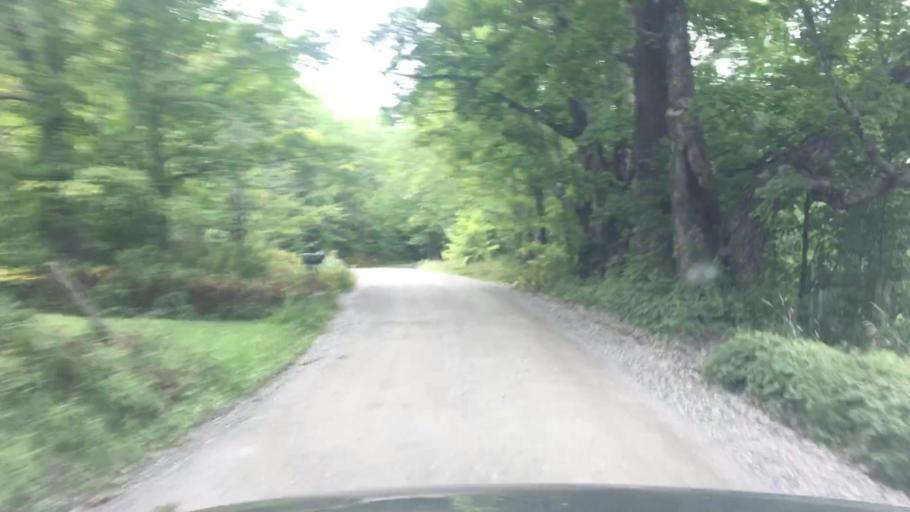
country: US
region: Vermont
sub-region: Windham County
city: Dover
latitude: 42.8510
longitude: -72.7758
